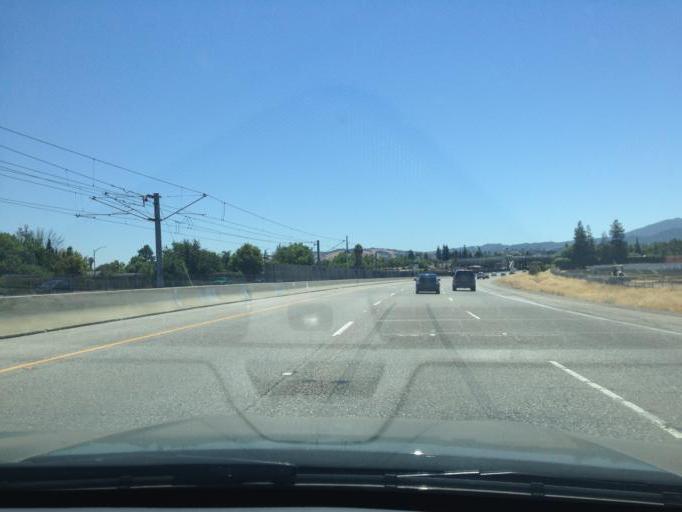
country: US
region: California
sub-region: Santa Clara County
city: Seven Trees
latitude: 37.2697
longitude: -121.8608
